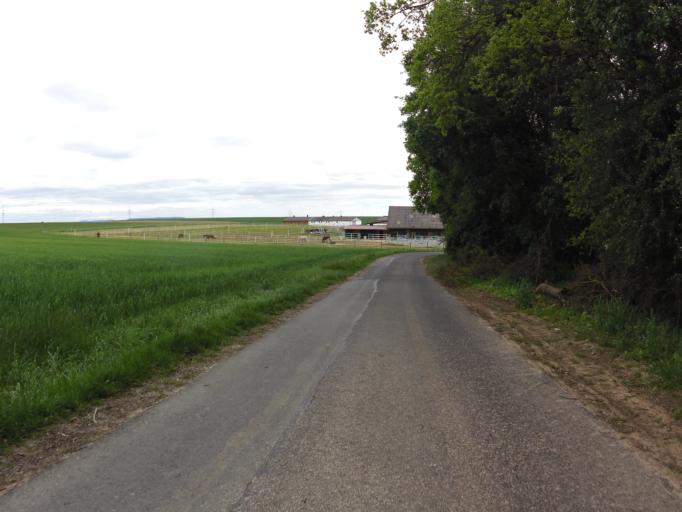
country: DE
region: Bavaria
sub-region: Regierungsbezirk Unterfranken
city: Oberpleichfeld
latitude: 49.8485
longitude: 10.0728
